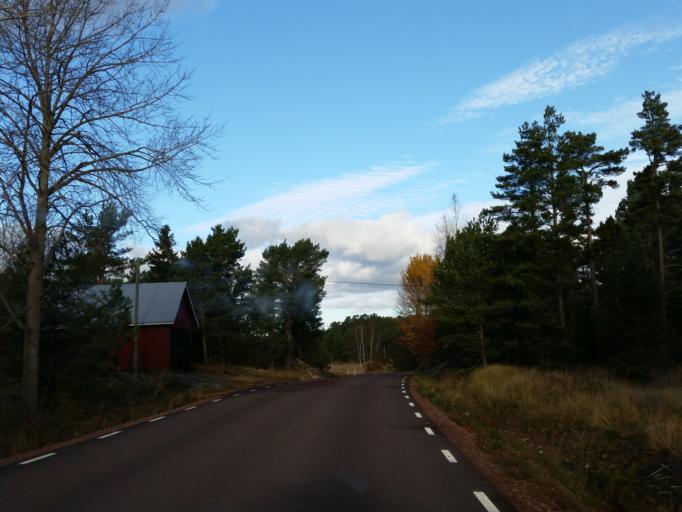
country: AX
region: Alands skaergard
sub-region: Foegloe
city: Foegloe
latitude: 60.0370
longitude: 20.5400
